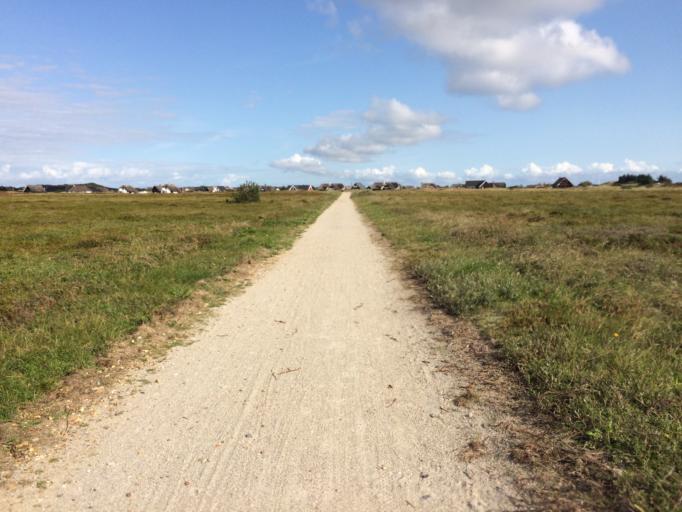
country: DK
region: Central Jutland
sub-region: Ringkobing-Skjern Kommune
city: Hvide Sande
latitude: 55.8829
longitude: 8.1689
